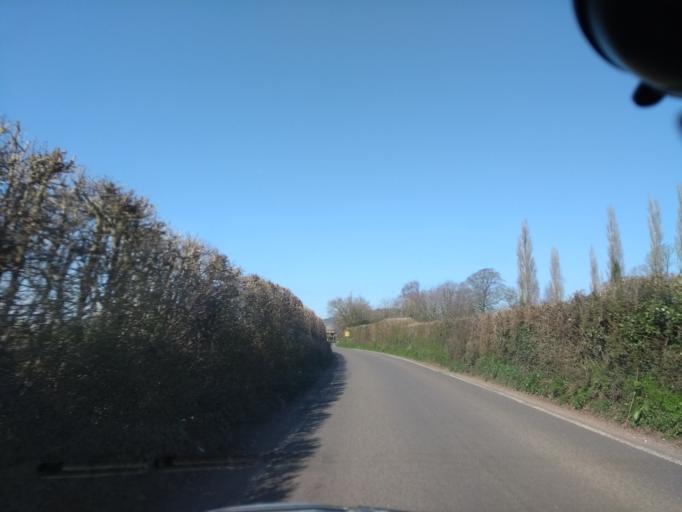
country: GB
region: England
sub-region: Somerset
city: Taunton
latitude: 51.0410
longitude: -3.1094
